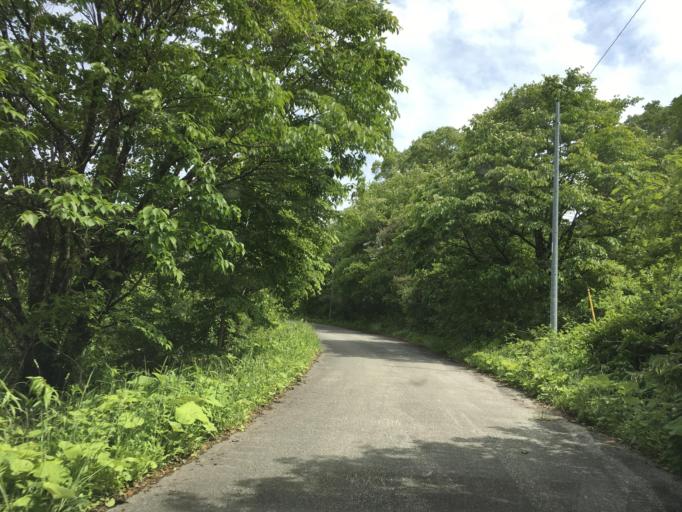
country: JP
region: Iwate
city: Mizusawa
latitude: 39.1346
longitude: 141.3146
